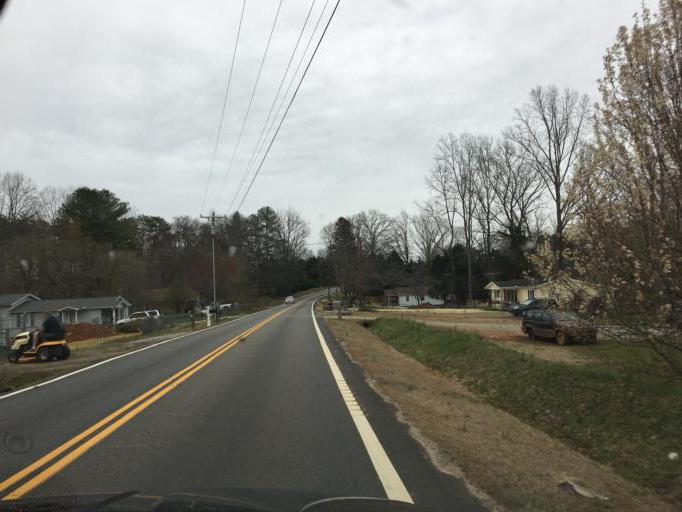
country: US
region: South Carolina
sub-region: Greenville County
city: Berea
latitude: 34.9307
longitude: -82.4967
